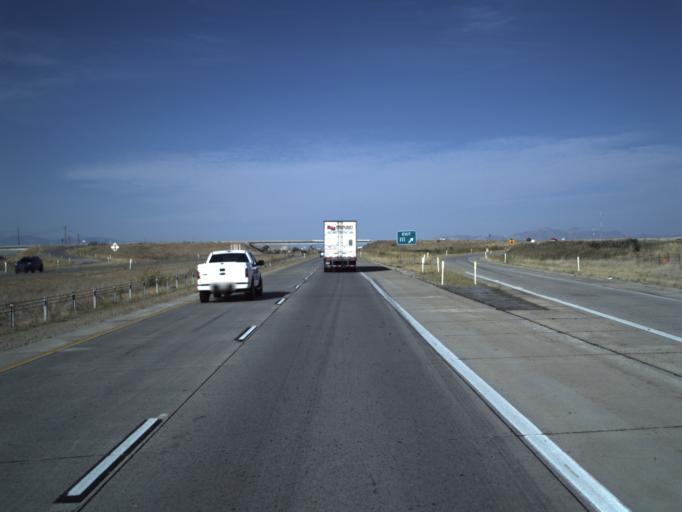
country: US
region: Utah
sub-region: Salt Lake County
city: Magna
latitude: 40.7712
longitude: -112.0565
